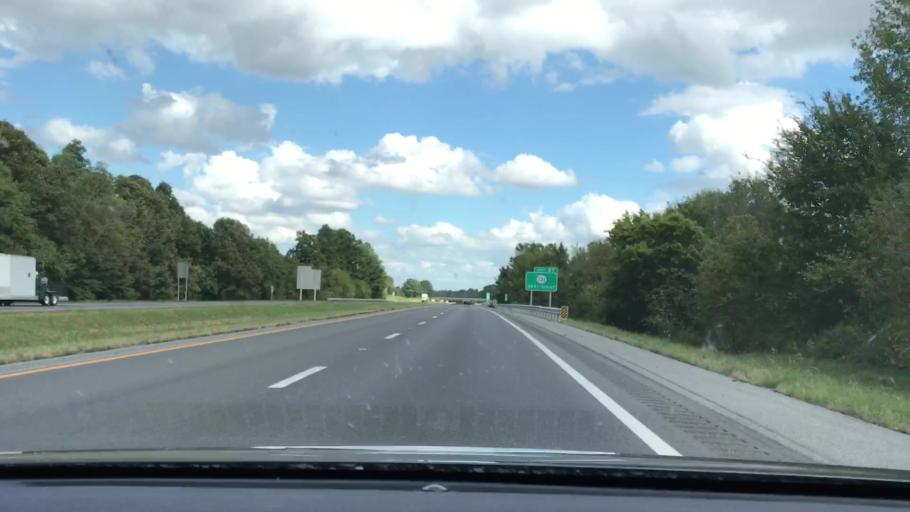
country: US
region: Kentucky
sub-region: Graves County
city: Mayfield
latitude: 36.7723
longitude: -88.6044
